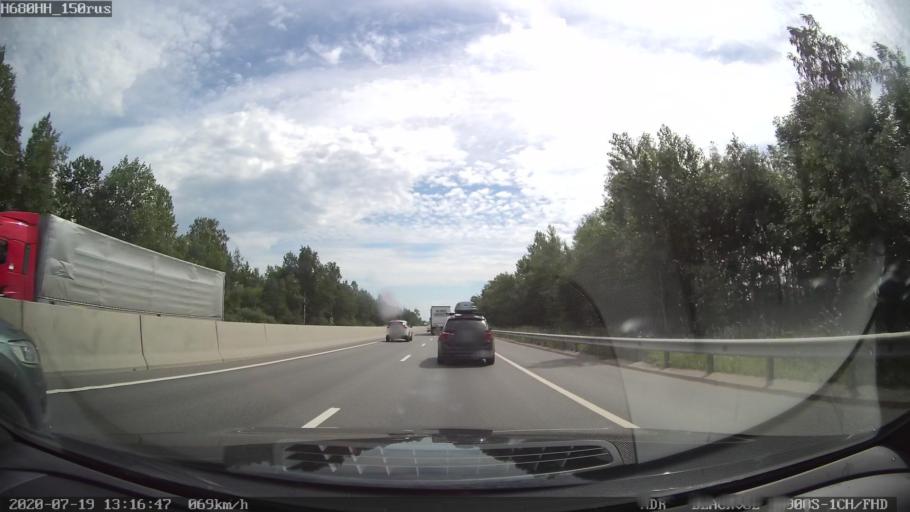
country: RU
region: St.-Petersburg
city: Kolpino
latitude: 59.7145
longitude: 30.5595
